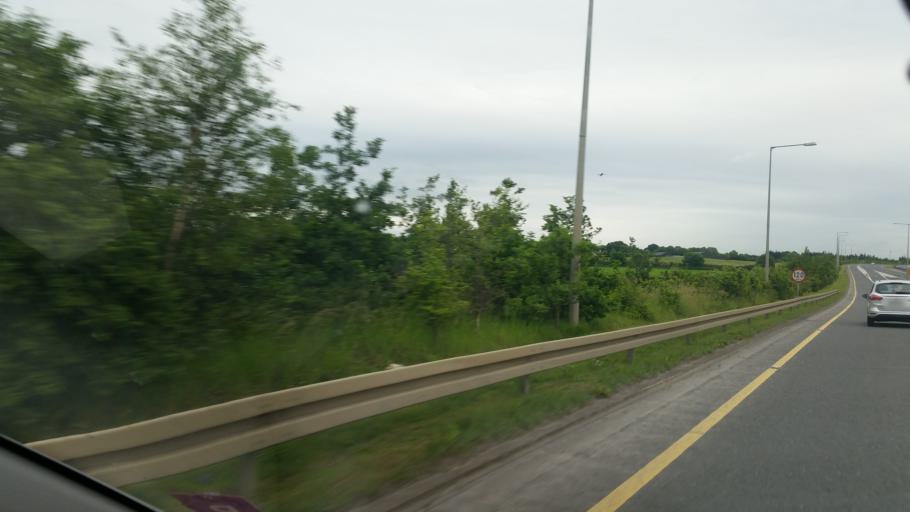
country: IE
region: Leinster
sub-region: Fingal County
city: Blanchardstown
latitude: 53.4314
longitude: -6.3419
